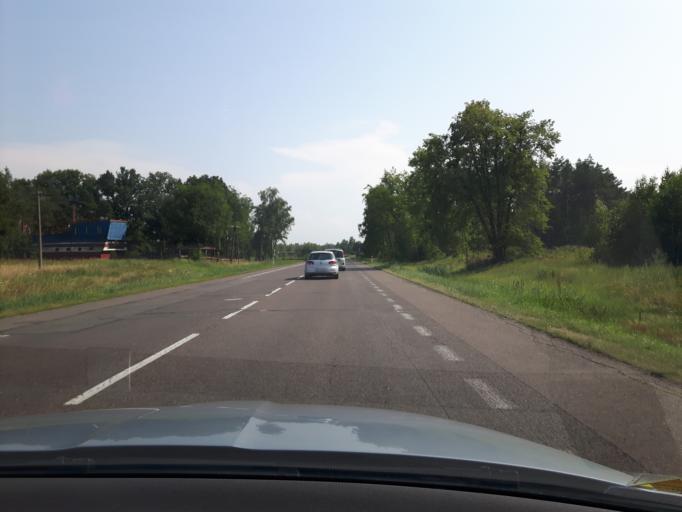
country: PL
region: Masovian Voivodeship
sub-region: Powiat plonski
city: Baboszewo
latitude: 52.7138
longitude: 20.3282
